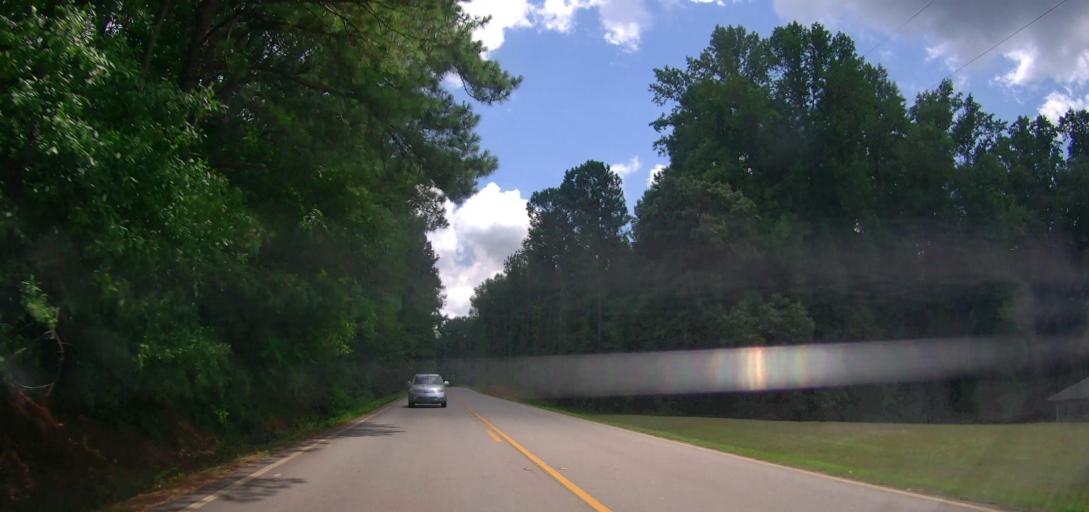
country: US
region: Georgia
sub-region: Troup County
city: Hogansville
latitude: 33.1331
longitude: -84.8327
